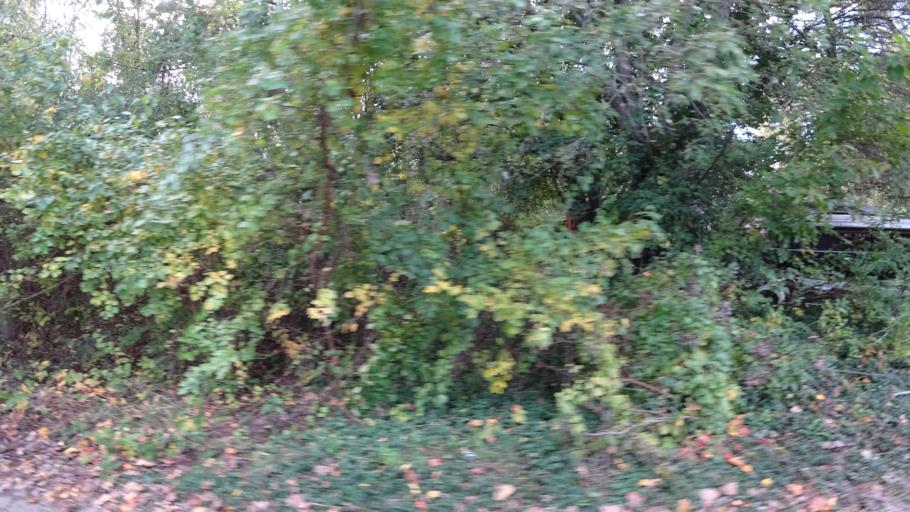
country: US
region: Michigan
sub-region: Saint Joseph County
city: Three Rivers
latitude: 41.9578
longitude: -85.5978
